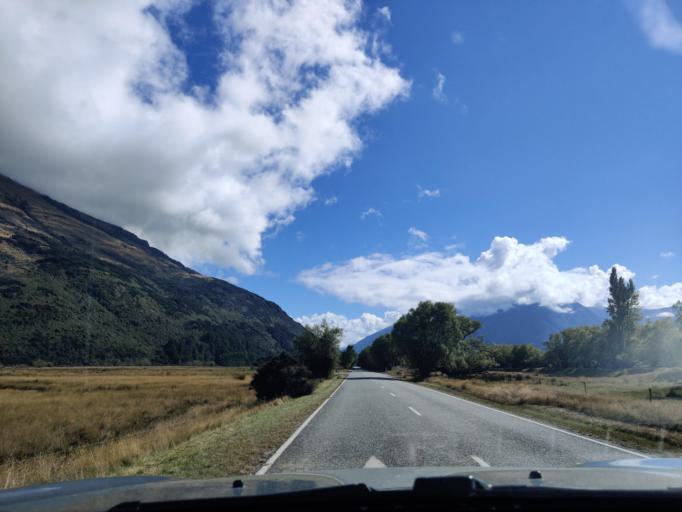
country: NZ
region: Otago
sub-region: Queenstown-Lakes District
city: Queenstown
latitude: -44.7842
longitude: 168.3948
